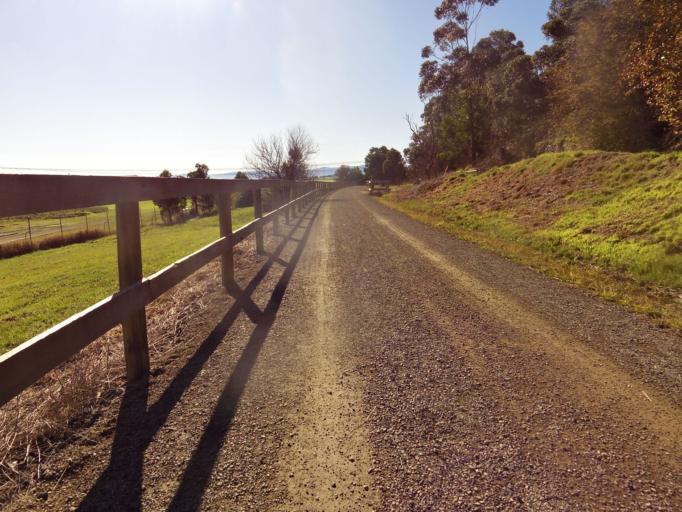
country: AU
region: Victoria
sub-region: Yarra Ranges
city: Lilydale
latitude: -37.7370
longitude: 145.3631
